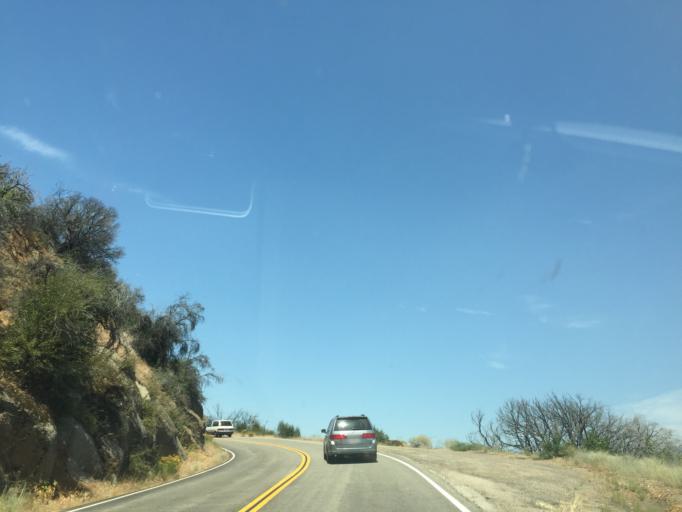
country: US
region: California
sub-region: Fresno County
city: Squaw Valley
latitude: 36.8335
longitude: -118.9001
